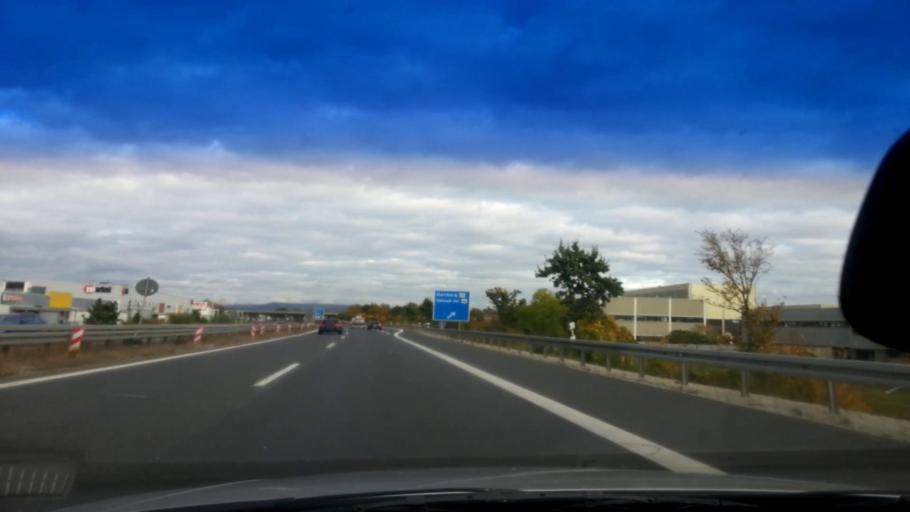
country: DE
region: Bavaria
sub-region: Upper Franconia
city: Hallstadt
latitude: 49.9233
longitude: 10.8943
